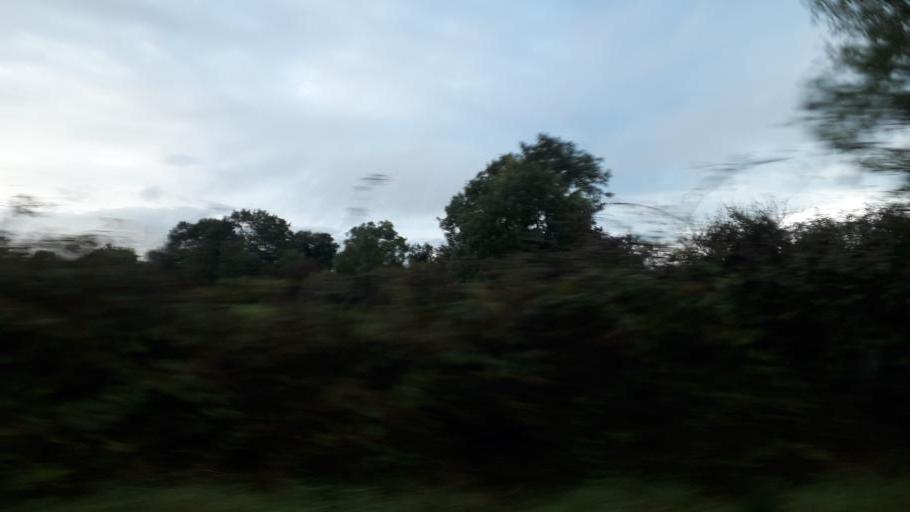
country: IE
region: Leinster
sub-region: An Longfort
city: Longford
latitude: 53.7255
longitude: -7.8635
